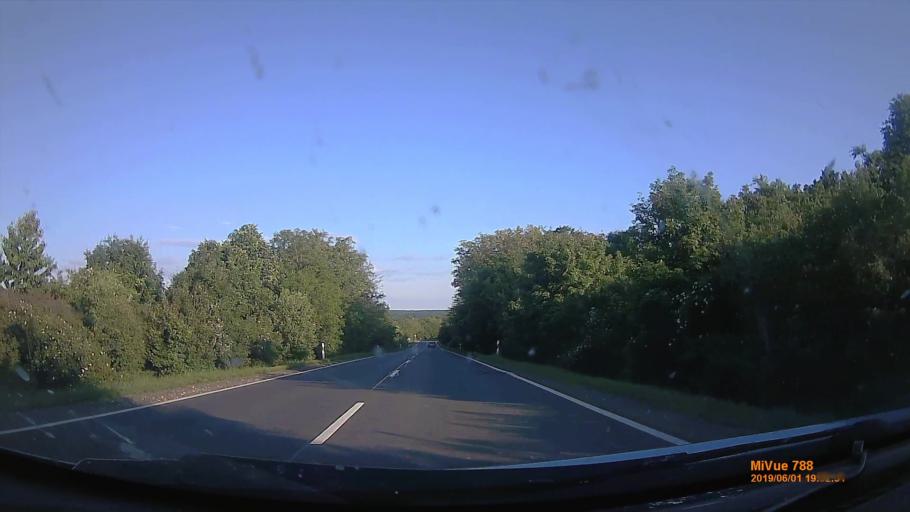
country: HU
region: Nograd
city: Nagyoroszi
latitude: 47.9835
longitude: 19.1146
